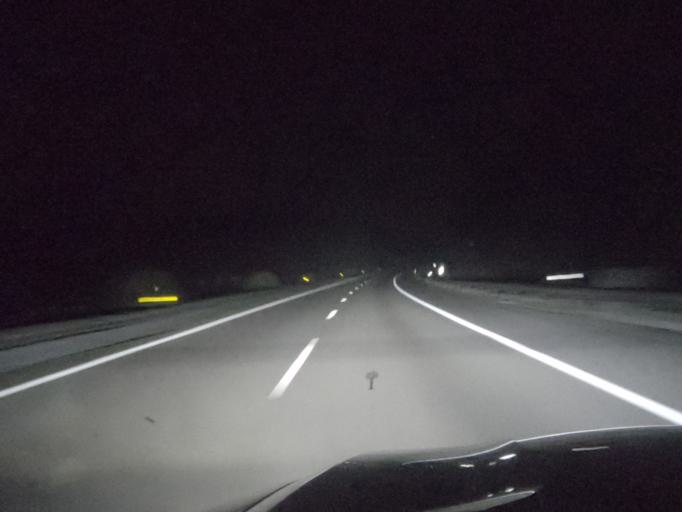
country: PT
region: Aveiro
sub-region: Oliveira do Bairro
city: Oliveira do Bairro
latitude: 40.4963
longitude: -8.5304
